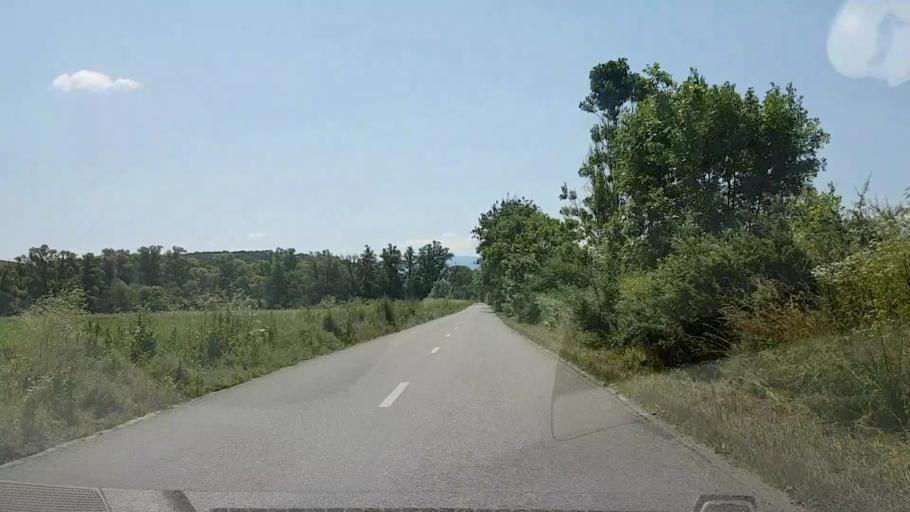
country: RO
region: Brasov
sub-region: Comuna Voila
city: Voila
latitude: 45.8577
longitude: 24.8283
